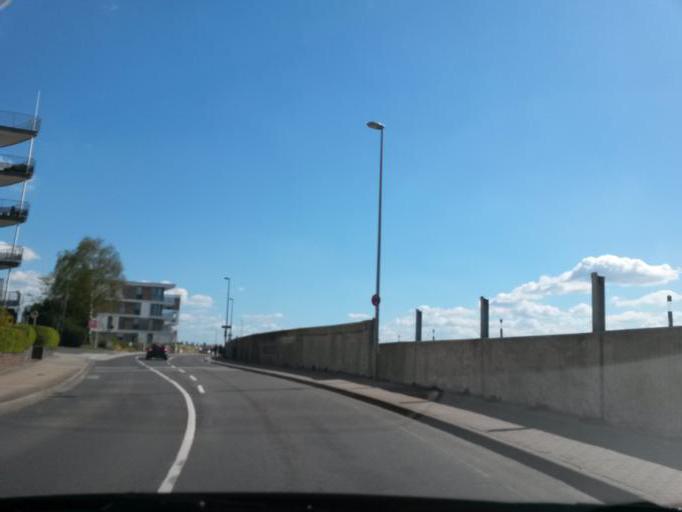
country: DE
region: Schleswig-Holstein
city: Wedel
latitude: 53.5709
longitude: 9.6991
